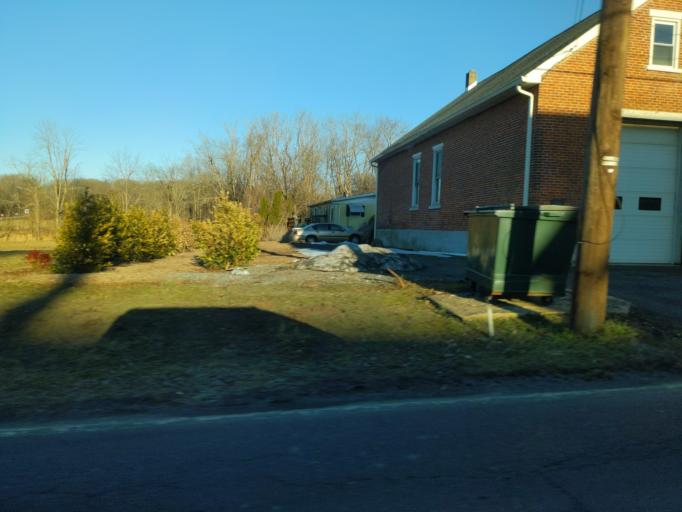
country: US
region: Pennsylvania
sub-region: Bucks County
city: Spinnerstown
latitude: 40.4381
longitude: -75.3992
